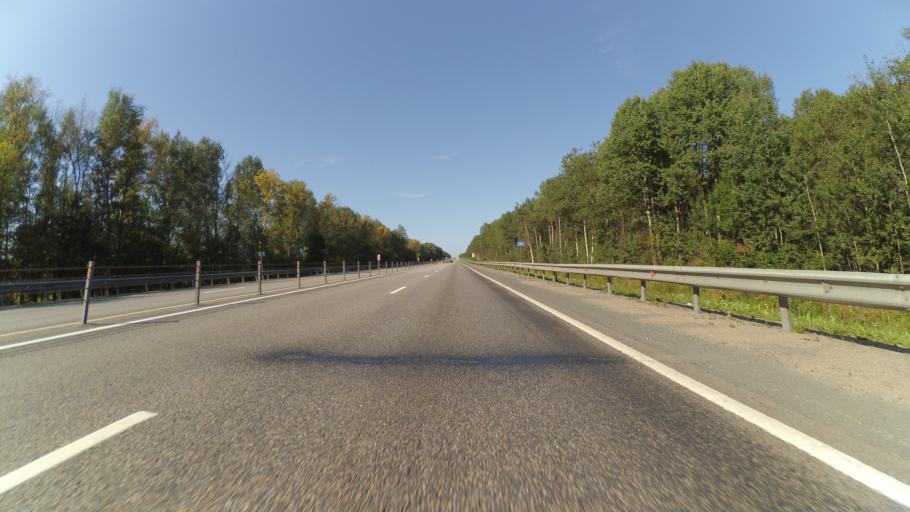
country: RU
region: Smolensk
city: Vyaz'ma
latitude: 55.2376
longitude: 34.2925
